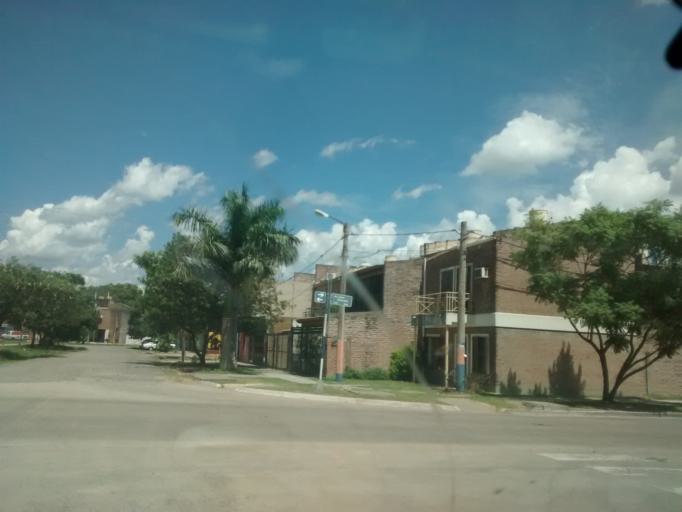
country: AR
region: Chaco
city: Resistencia
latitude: -27.4710
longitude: -58.9867
